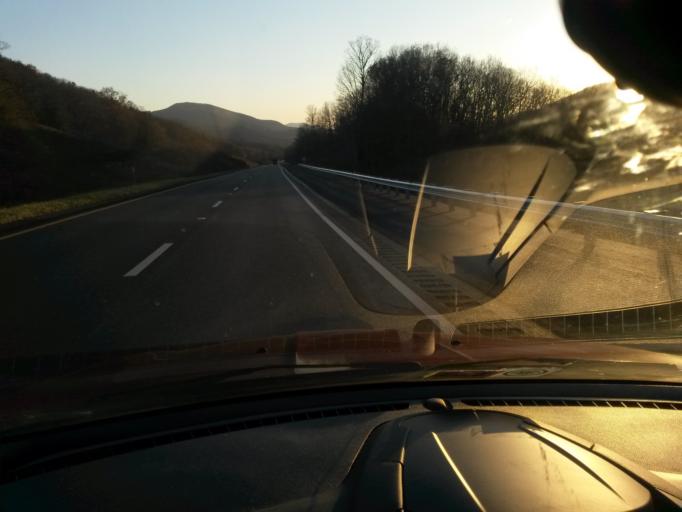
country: US
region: Virginia
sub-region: City of Lexington
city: Lexington
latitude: 37.8599
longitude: -79.6264
